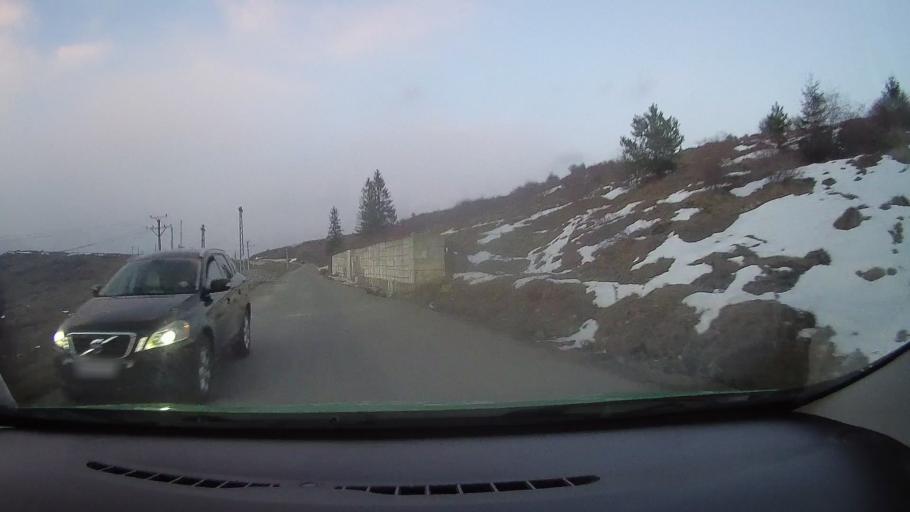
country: RO
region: Prahova
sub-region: Comuna Secaria
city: Secaria
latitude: 45.2799
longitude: 25.6999
